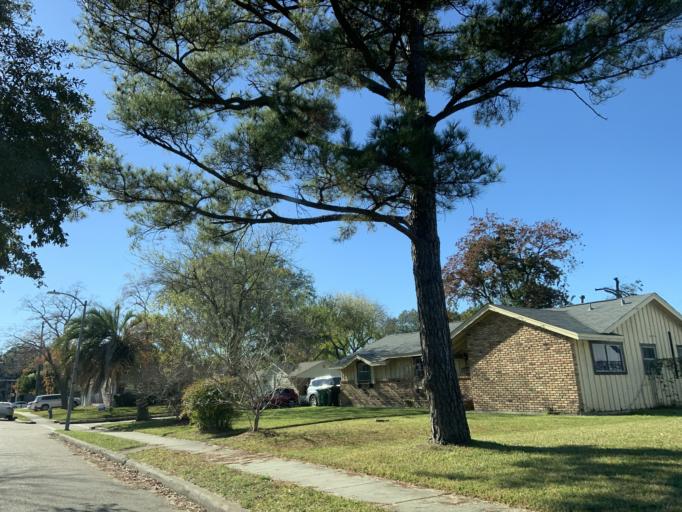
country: US
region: Texas
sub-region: Harris County
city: Bellaire
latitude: 29.6979
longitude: -95.5130
